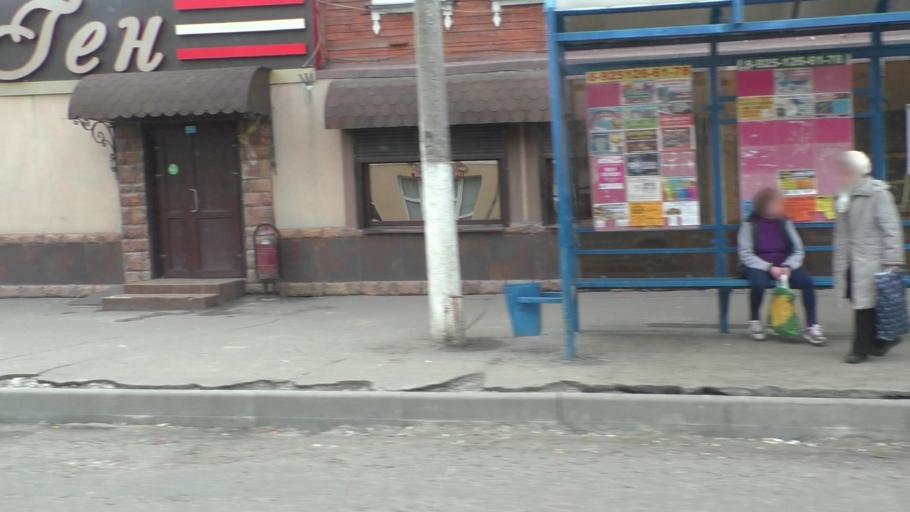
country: RU
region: Moskovskaya
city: Yegor'yevsk
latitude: 55.3860
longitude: 39.0313
